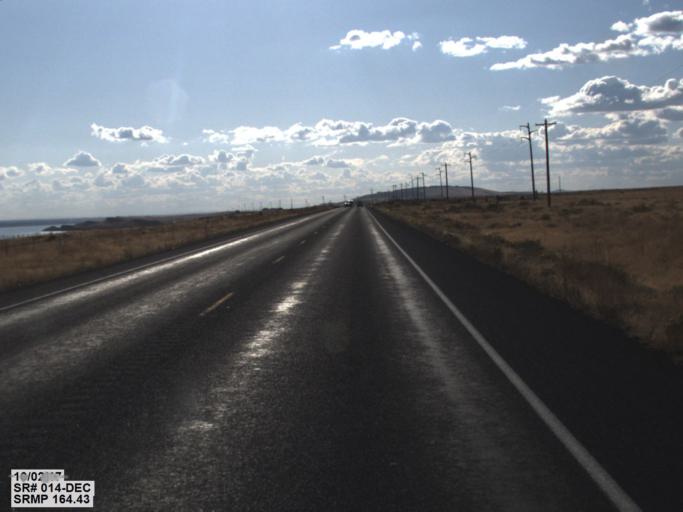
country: US
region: Oregon
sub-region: Morrow County
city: Boardman
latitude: 45.9169
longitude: -119.6540
